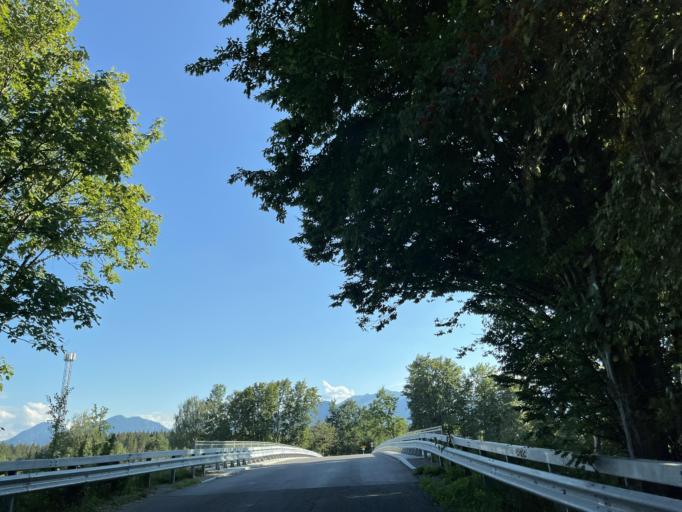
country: DE
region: Bavaria
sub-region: Upper Bavaria
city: Kolbermoor
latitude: 47.8135
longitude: 12.0763
